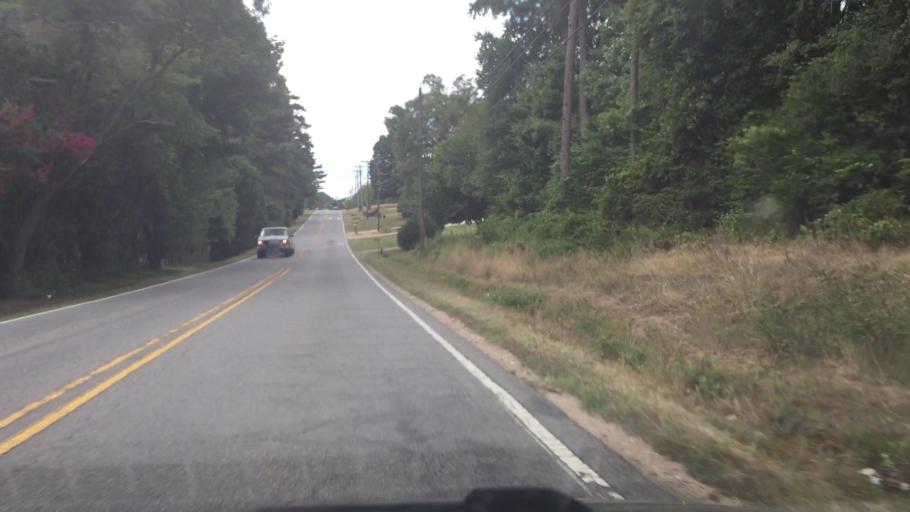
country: US
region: North Carolina
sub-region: Rowan County
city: Enochville
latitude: 35.5130
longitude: -80.6717
